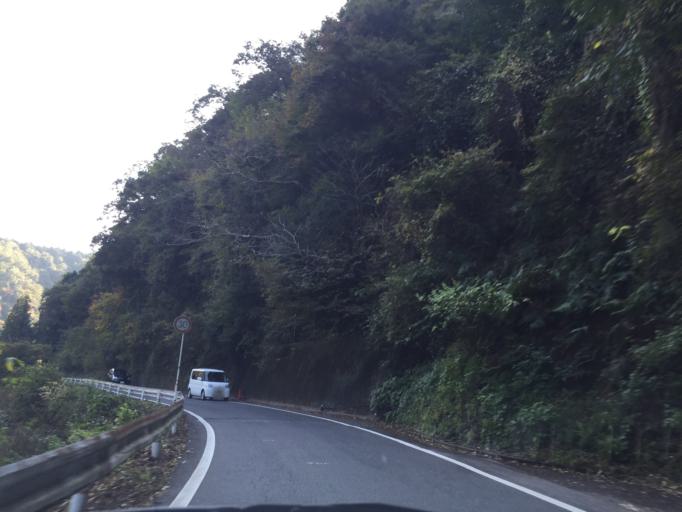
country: JP
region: Gifu
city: Minokamo
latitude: 35.5511
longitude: 137.1159
